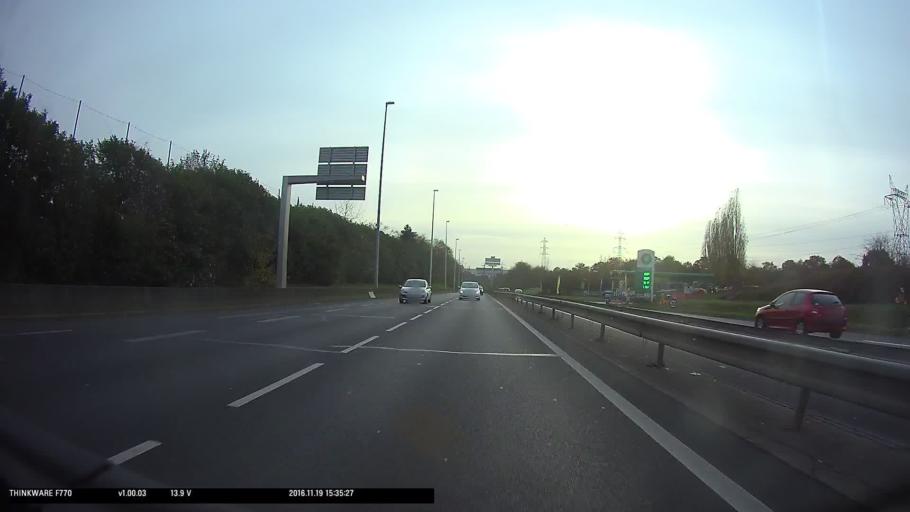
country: FR
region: Ile-de-France
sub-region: Departement du Val-d'Oise
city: Pontoise
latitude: 49.0619
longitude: 2.0856
